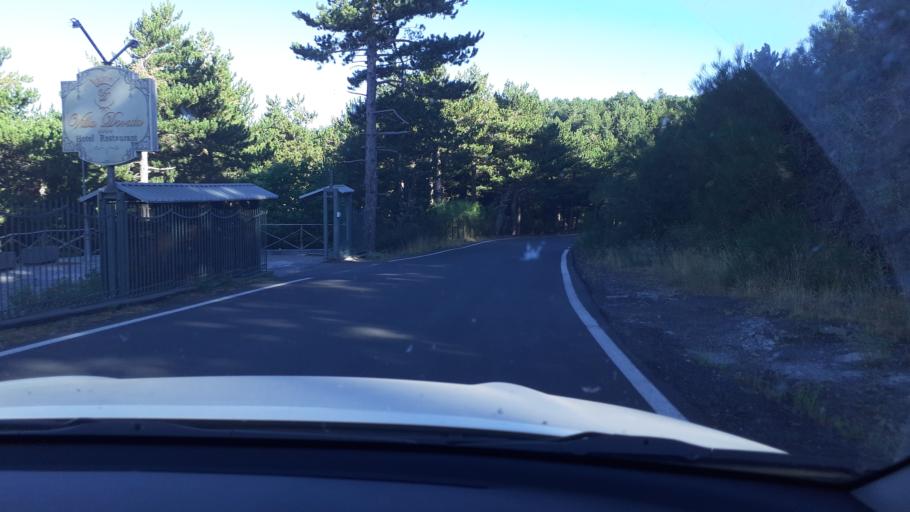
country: IT
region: Sicily
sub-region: Catania
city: Ragalna
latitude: 37.6885
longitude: 14.9768
